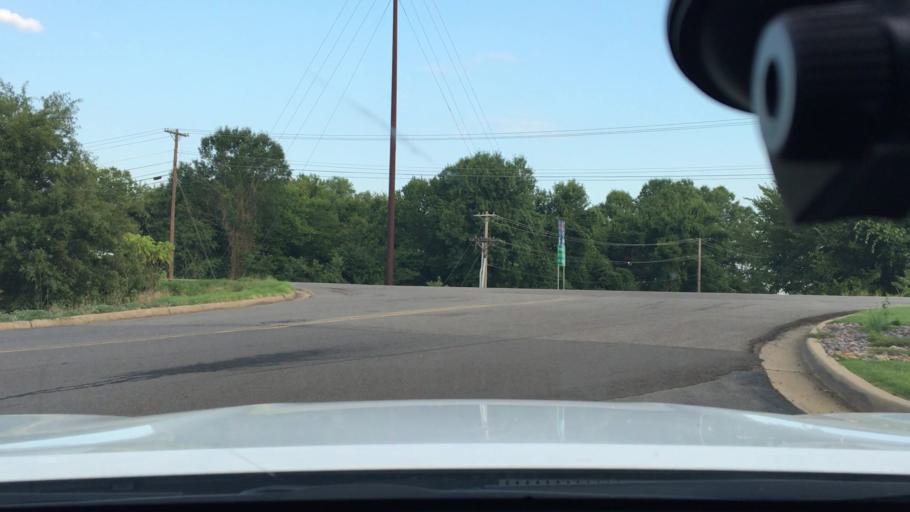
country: US
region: Arkansas
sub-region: Johnson County
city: Clarksville
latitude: 35.4664
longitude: -93.5193
